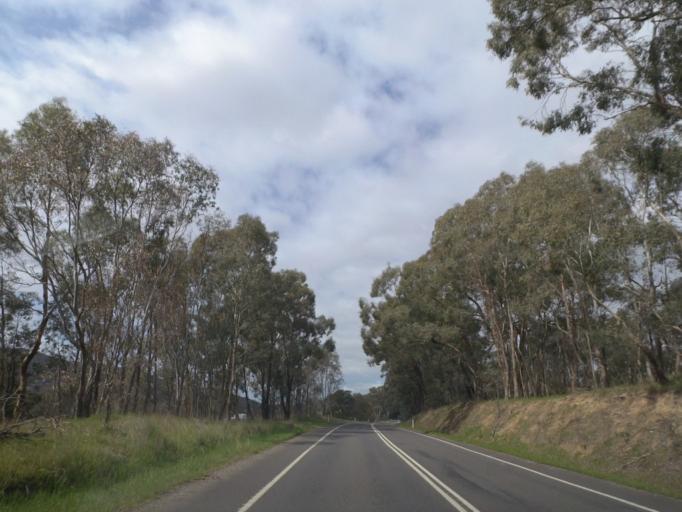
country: AU
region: Victoria
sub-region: Murrindindi
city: Kinglake West
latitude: -37.1275
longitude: 145.2235
